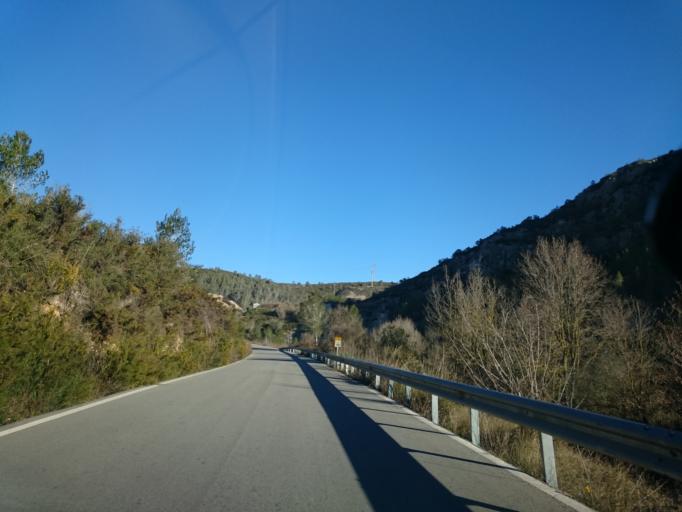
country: ES
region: Catalonia
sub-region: Provincia de Barcelona
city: Vilafranca del Penedes
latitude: 41.3075
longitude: 1.7255
